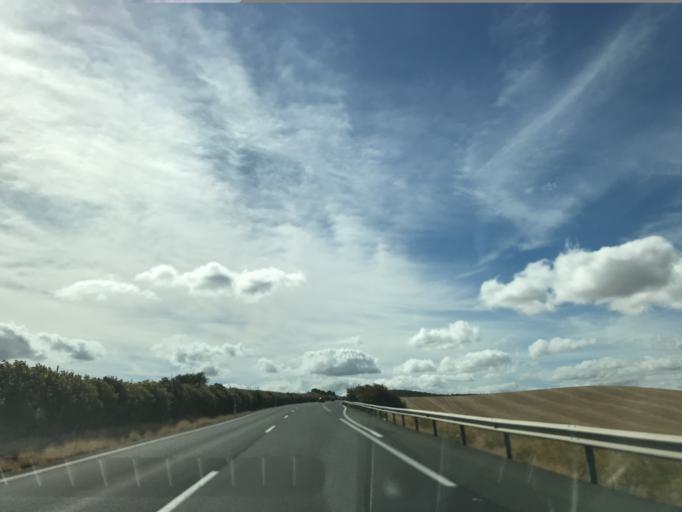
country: ES
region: Andalusia
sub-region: Province of Cordoba
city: La Victoria
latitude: 37.7311
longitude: -4.8543
